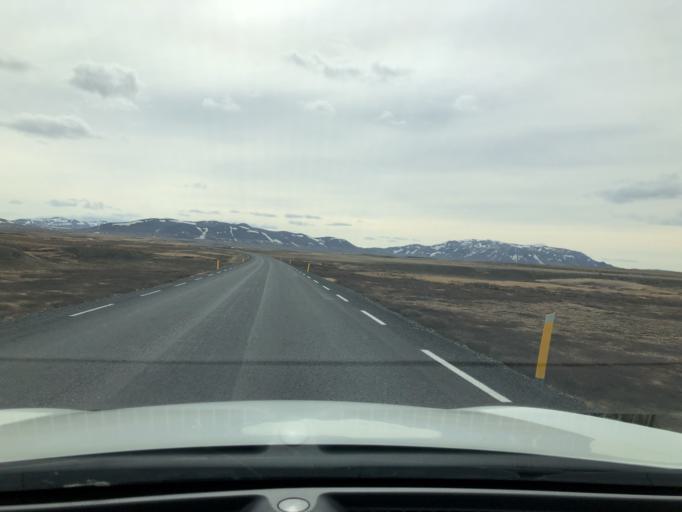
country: IS
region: Northeast
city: Laugar
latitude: 65.6006
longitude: -16.1372
